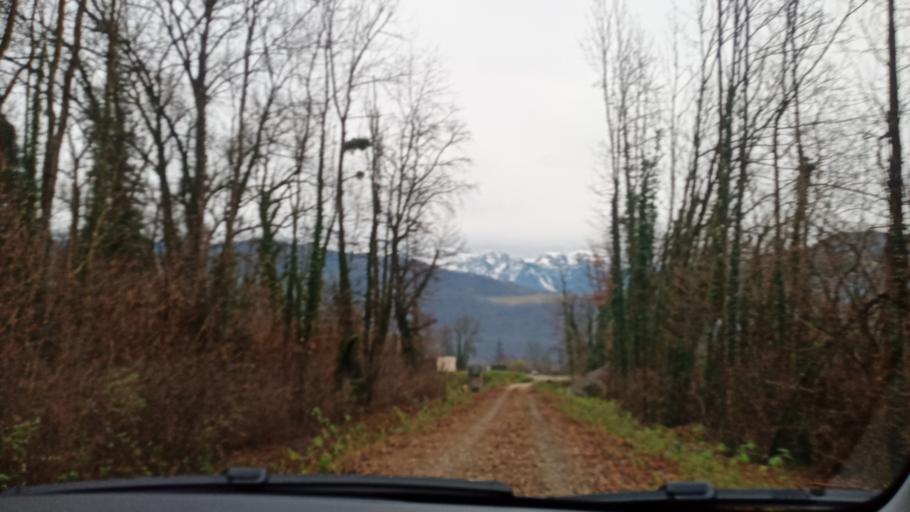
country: FR
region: Rhone-Alpes
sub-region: Departement de l'Isere
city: Domene
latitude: 45.2172
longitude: 5.8334
